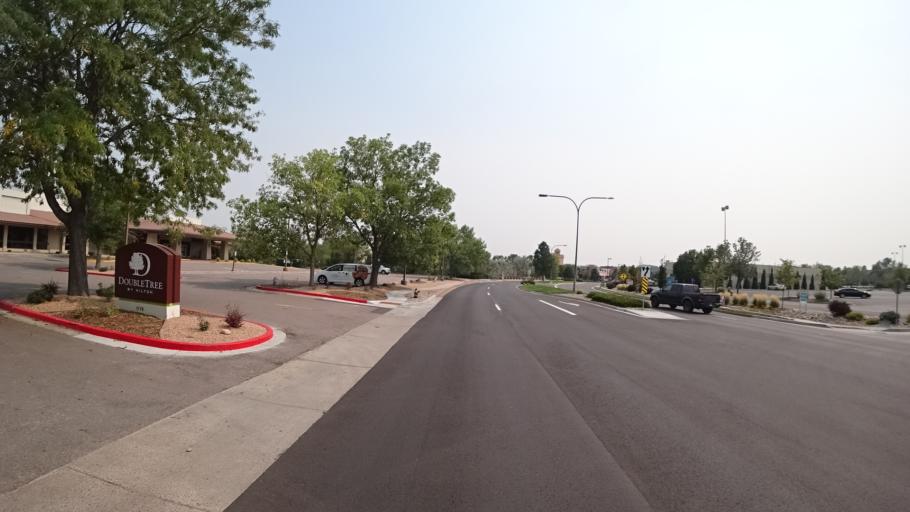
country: US
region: Colorado
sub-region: El Paso County
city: Stratmoor
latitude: 38.7938
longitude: -104.8002
